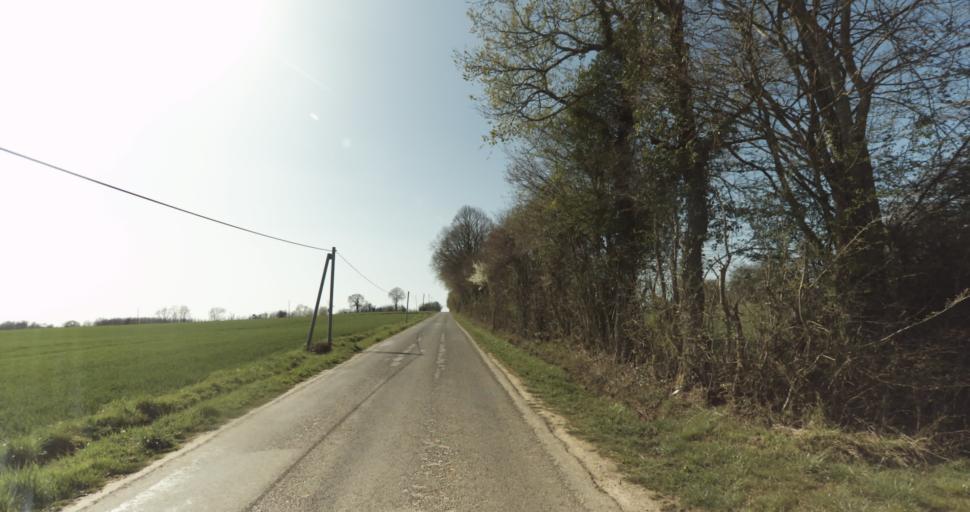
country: FR
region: Lower Normandy
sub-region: Departement du Calvados
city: Saint-Pierre-sur-Dives
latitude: 48.9393
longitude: 0.0041
